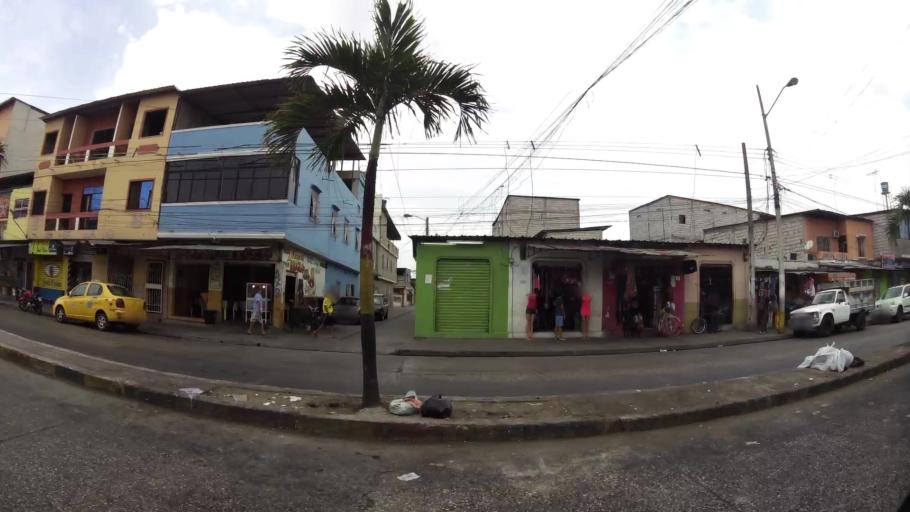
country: EC
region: Guayas
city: Guayaquil
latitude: -2.2294
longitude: -79.9067
